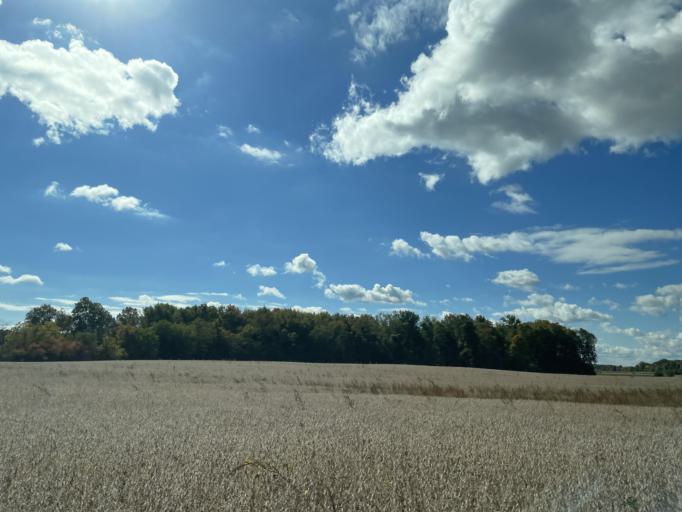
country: US
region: Indiana
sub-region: Allen County
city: Fort Wayne
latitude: 41.1183
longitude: -85.2423
